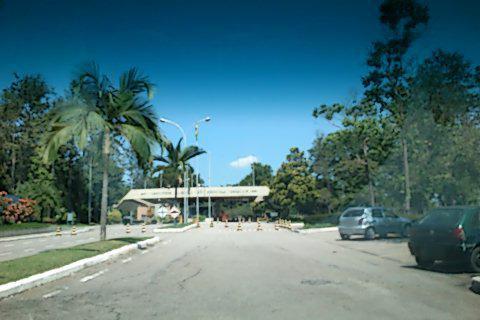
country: BR
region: Sao Paulo
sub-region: Sao Jose Dos Campos
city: Sao Jose dos Campos
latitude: -23.2064
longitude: -45.8611
